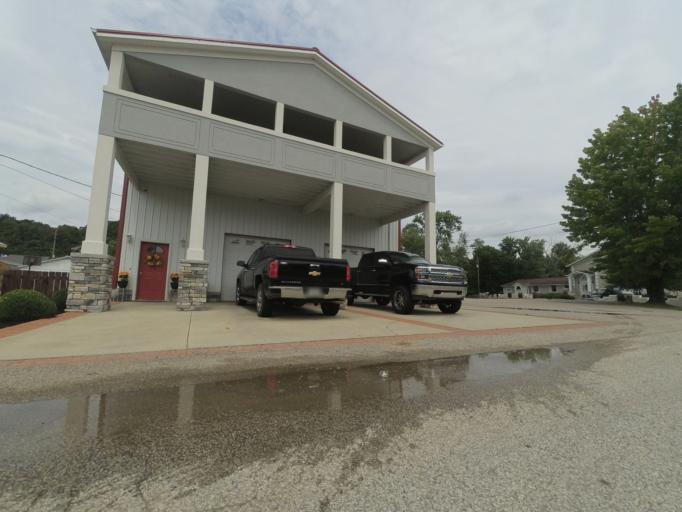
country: US
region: West Virginia
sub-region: Cabell County
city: Huntington
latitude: 38.4252
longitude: -82.4636
